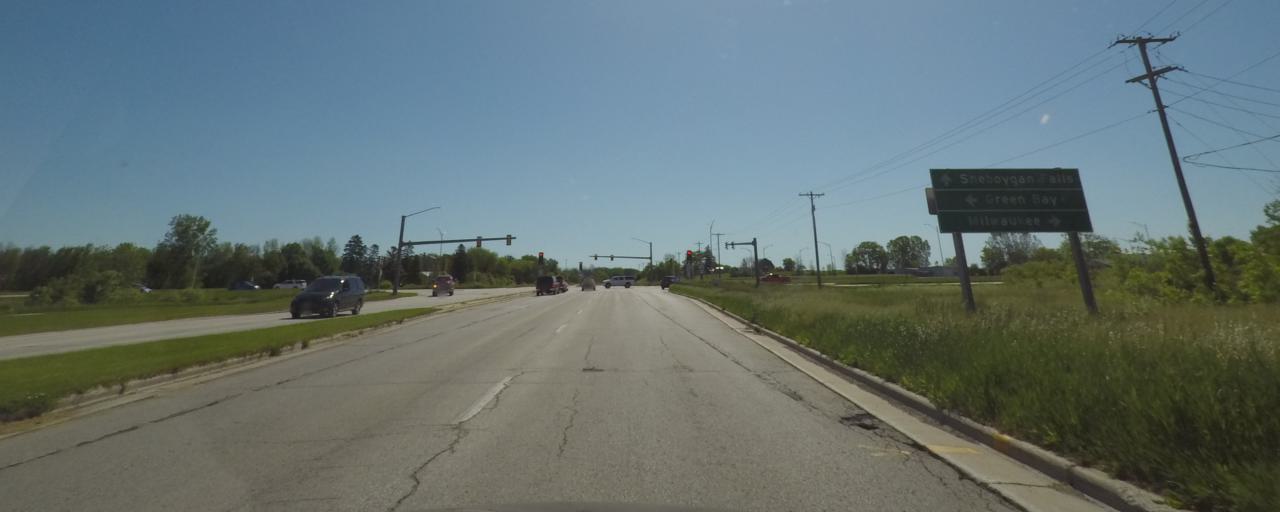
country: US
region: Wisconsin
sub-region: Sheboygan County
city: Plymouth
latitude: 43.7471
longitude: -87.9428
